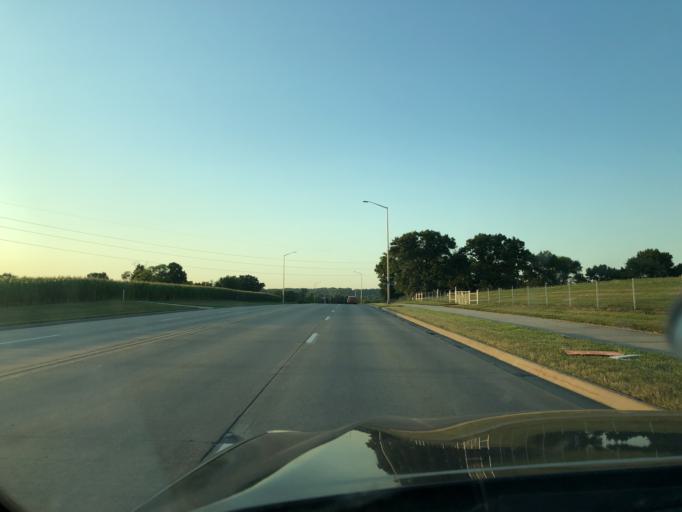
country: US
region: Kansas
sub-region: Leavenworth County
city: Leavenworth
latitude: 39.2718
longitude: -94.9468
